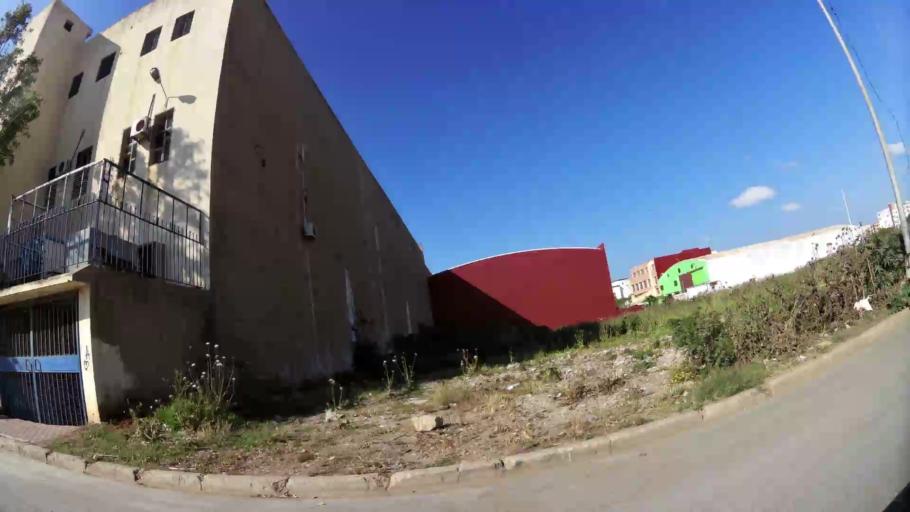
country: MA
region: Rabat-Sale-Zemmour-Zaer
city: Sale
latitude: 34.0524
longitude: -6.8094
